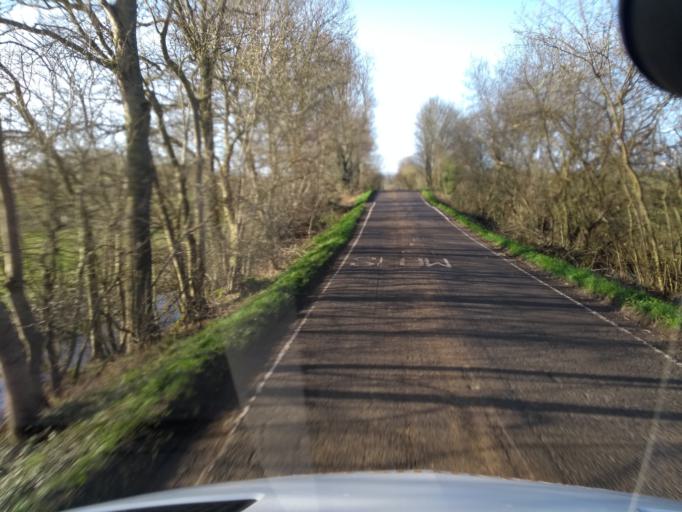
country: GB
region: England
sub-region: Somerset
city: Wedmore
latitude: 51.1588
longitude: -2.8317
